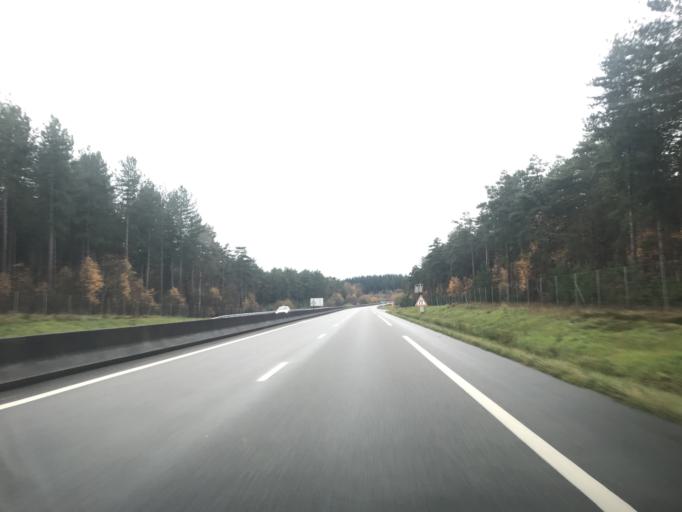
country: FR
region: Haute-Normandie
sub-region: Departement de l'Eure
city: Brionne
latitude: 49.1749
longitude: 0.7443
